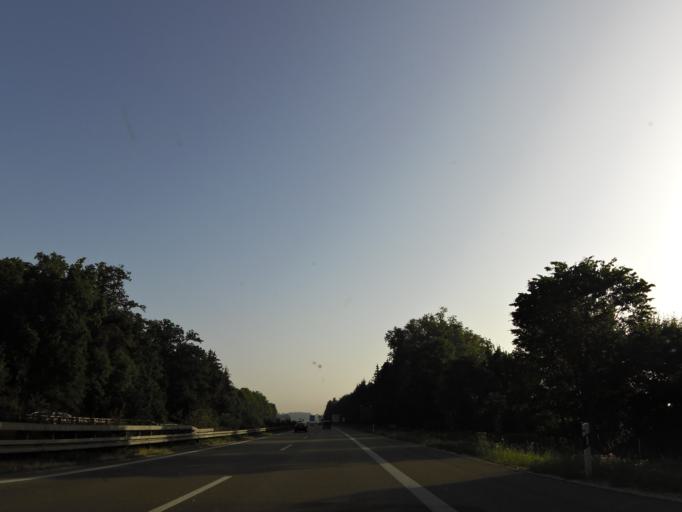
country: DE
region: Bavaria
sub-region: Swabia
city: Holzheim
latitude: 48.4017
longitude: 10.0921
